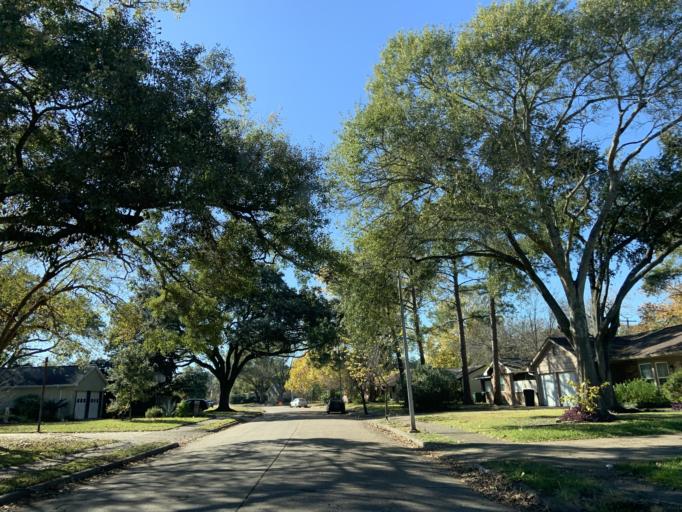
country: US
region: Texas
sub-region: Harris County
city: Bellaire
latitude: 29.6963
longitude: -95.5101
